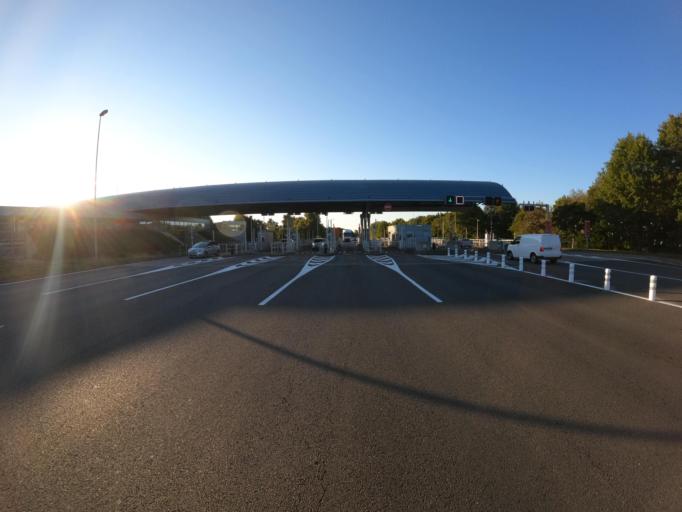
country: FR
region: Pays de la Loire
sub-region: Departement de la Vendee
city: Bouffere
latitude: 46.9593
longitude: -1.3526
